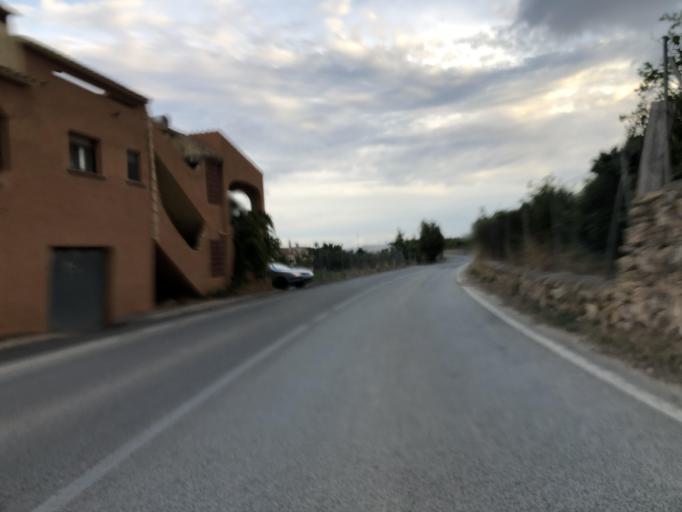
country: ES
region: Valencia
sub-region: Provincia de Alicante
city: Polop
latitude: 38.6319
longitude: -0.1431
